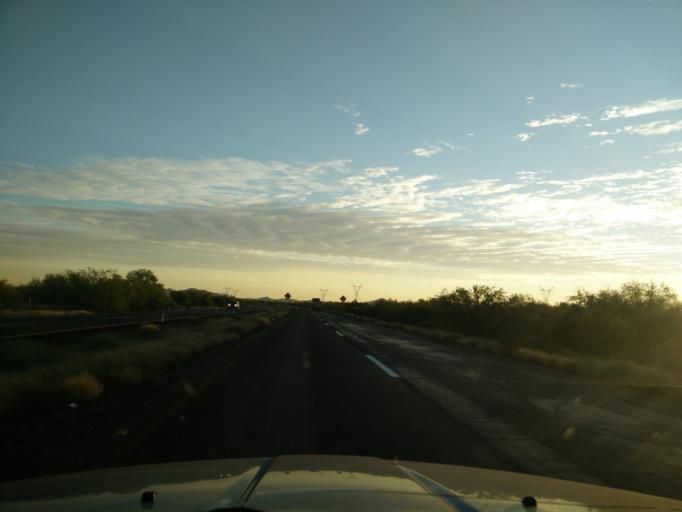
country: MX
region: Sonora
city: Hermosillo
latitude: 28.6612
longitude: -111.0008
